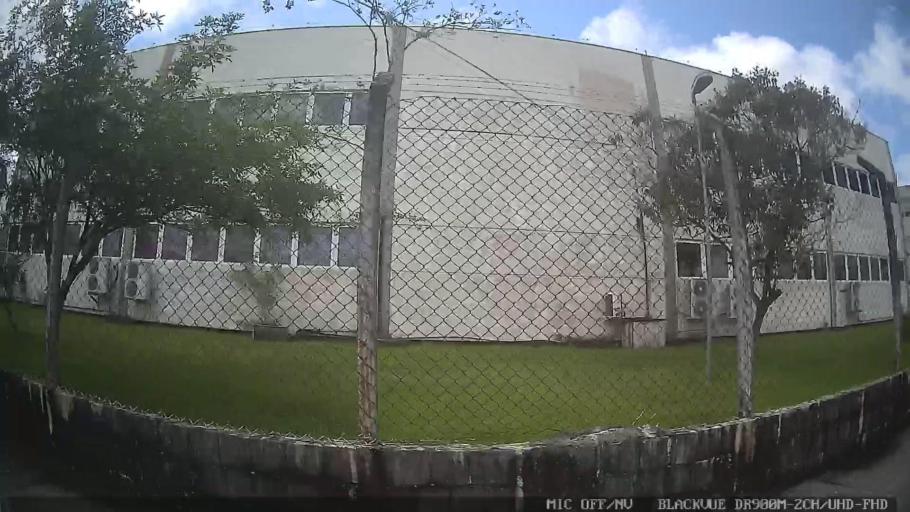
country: BR
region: Sao Paulo
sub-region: Caraguatatuba
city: Caraguatatuba
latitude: -23.6139
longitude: -45.3795
